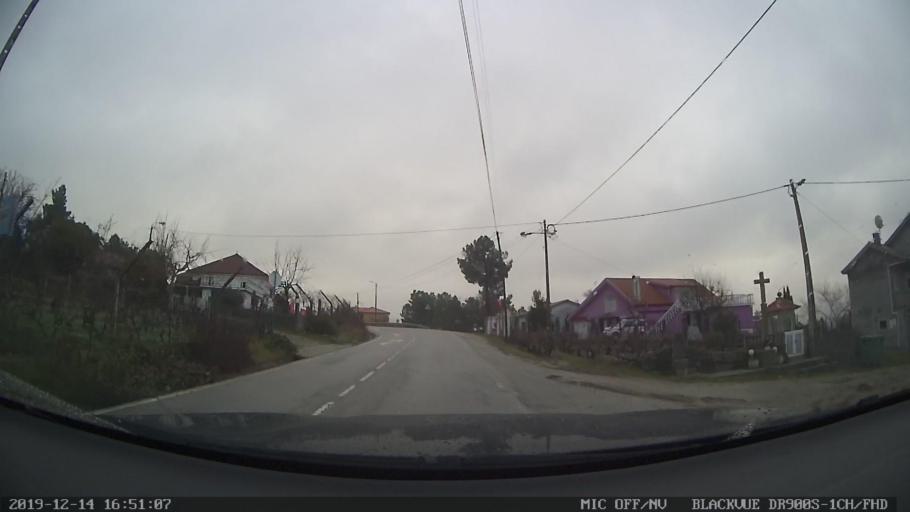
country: PT
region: Vila Real
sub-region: Murca
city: Murca
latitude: 41.4213
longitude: -7.5050
